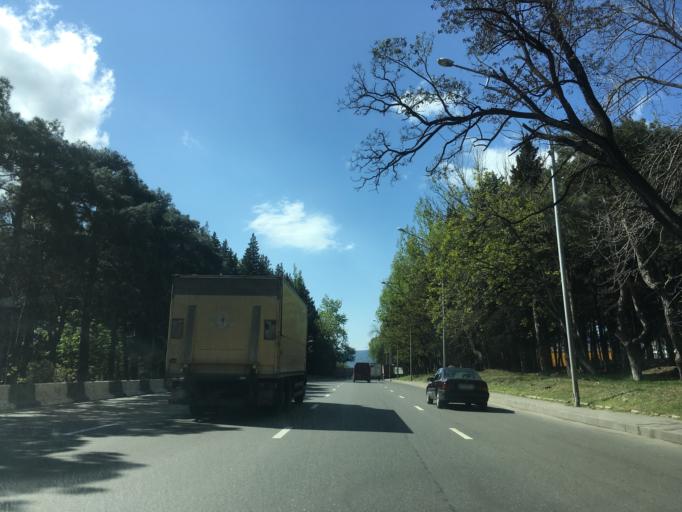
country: GE
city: Zahesi
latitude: 41.8023
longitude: 44.7706
